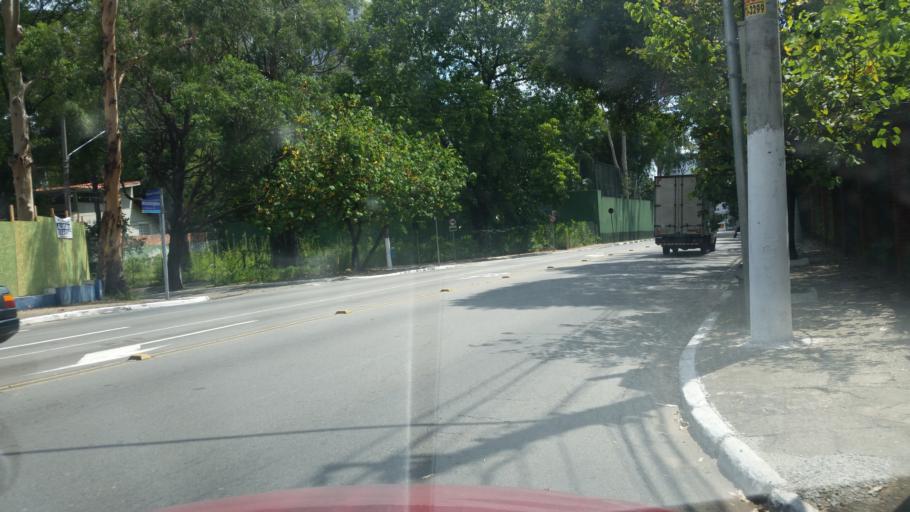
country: BR
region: Sao Paulo
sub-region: Diadema
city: Diadema
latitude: -23.6536
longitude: -46.6897
